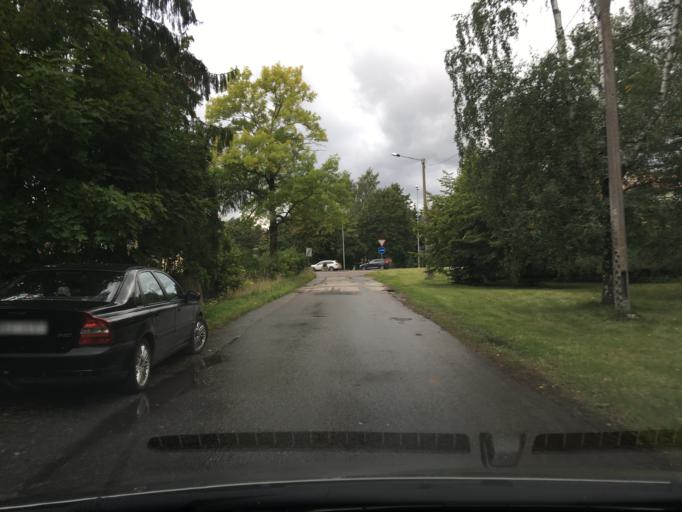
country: EE
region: Harju
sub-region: Tallinna linn
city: Tallinn
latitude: 59.3884
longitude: 24.7209
